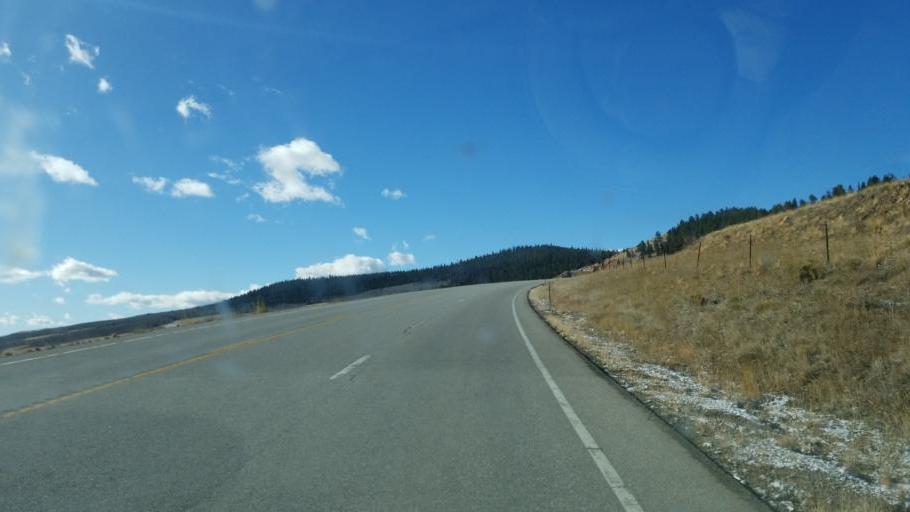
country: US
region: Colorado
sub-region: Park County
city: Fairplay
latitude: 39.2722
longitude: -105.9532
